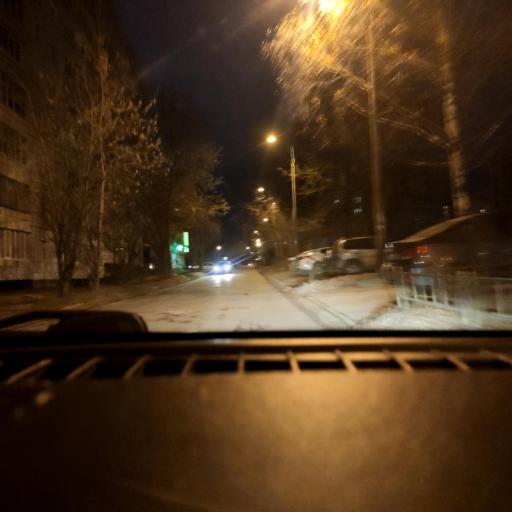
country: RU
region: Perm
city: Perm
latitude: 57.9716
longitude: 56.2251
